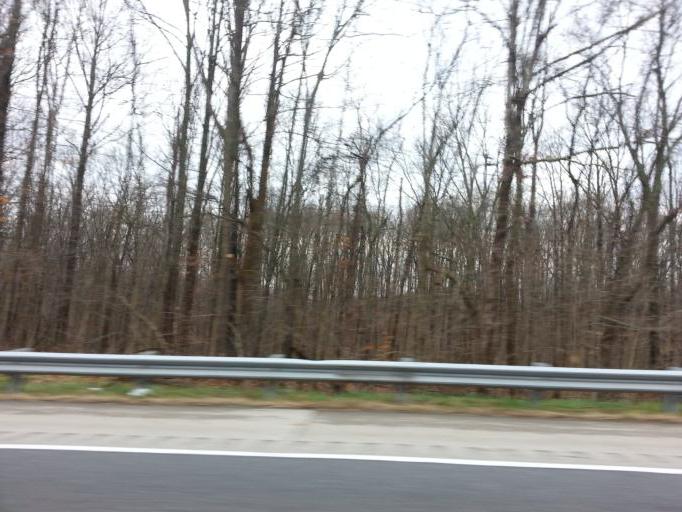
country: US
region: Indiana
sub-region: Ripley County
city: Sunman
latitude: 39.2803
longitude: -85.1152
